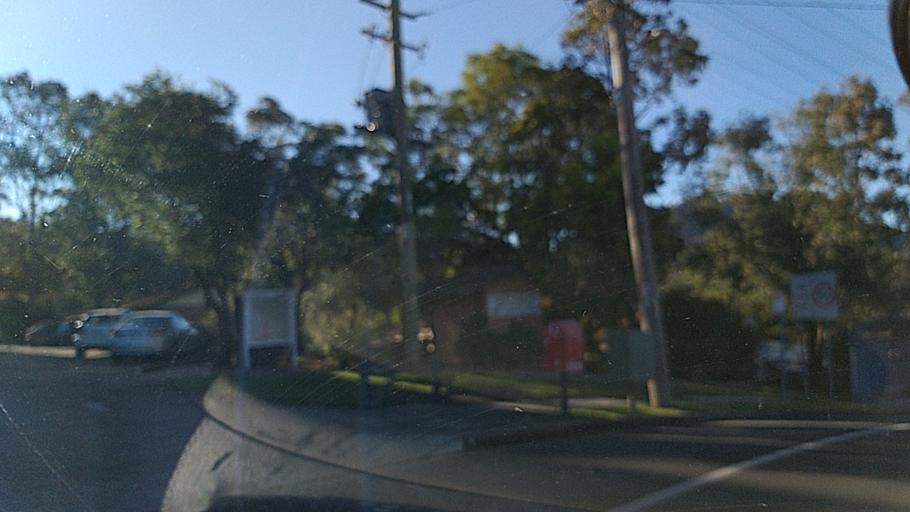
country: AU
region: New South Wales
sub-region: Wollongong
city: Mount Keira
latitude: -34.4255
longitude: 150.8463
